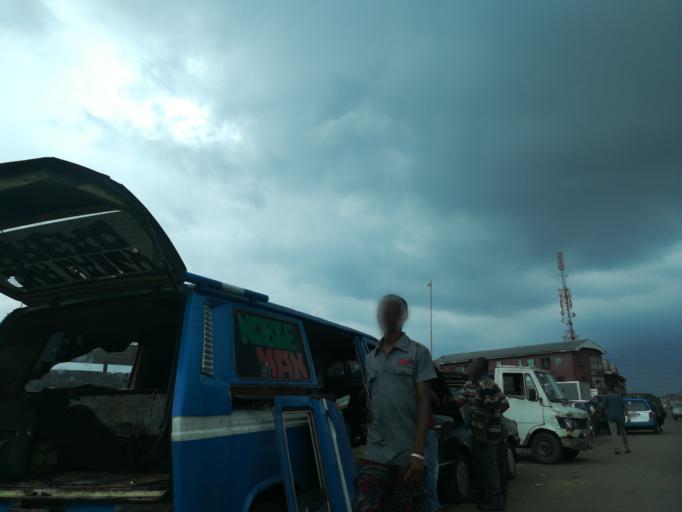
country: NG
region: Rivers
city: Port Harcourt
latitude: 4.7956
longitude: 6.9879
